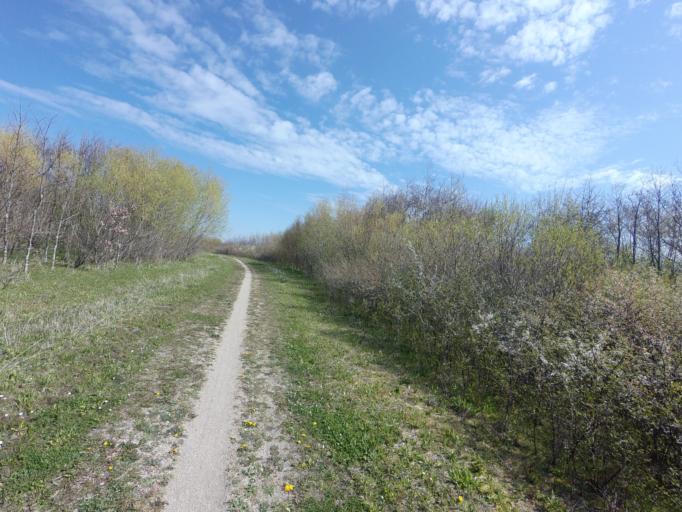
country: NL
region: Zeeland
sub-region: Gemeente Vlissingen
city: Vlissingen
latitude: 51.5157
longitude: 3.4606
